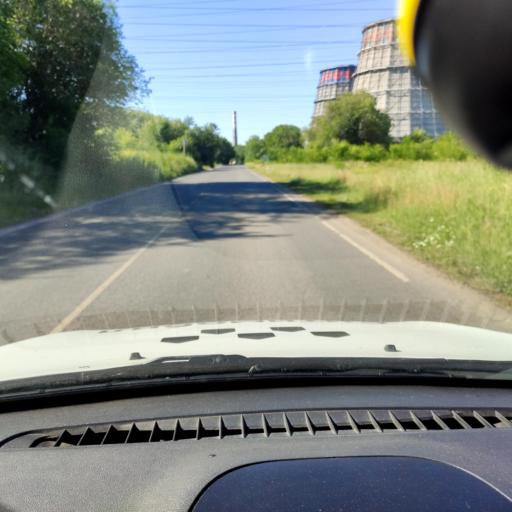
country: RU
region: Samara
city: Tol'yatti
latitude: 53.5788
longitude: 49.2554
